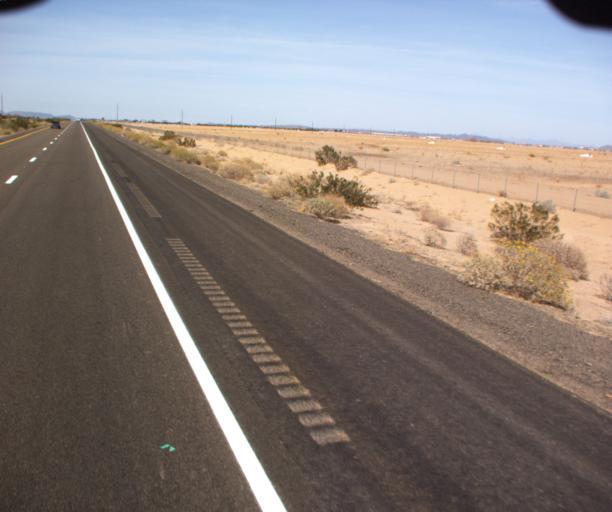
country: US
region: Arizona
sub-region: Yuma County
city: Fortuna Foothills
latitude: 32.6449
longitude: -114.5213
